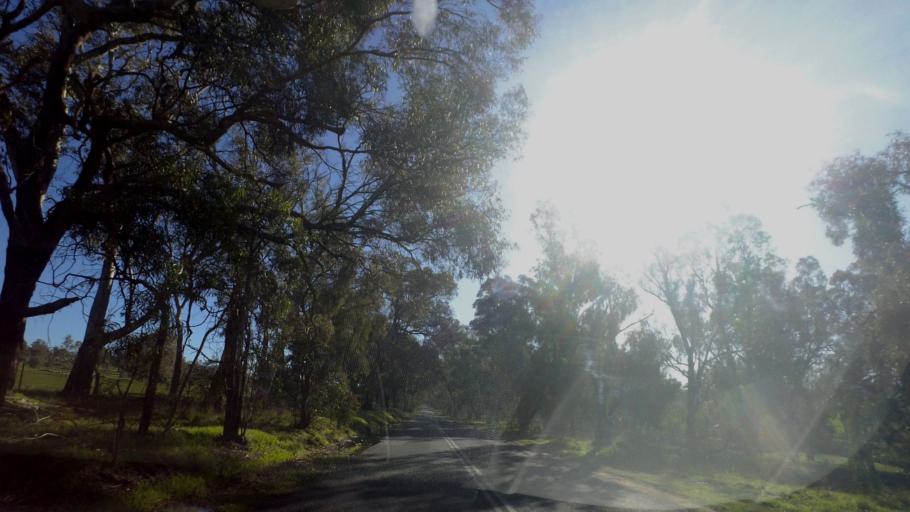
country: AU
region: Victoria
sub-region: Mount Alexander
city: Castlemaine
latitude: -36.9597
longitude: 144.3502
